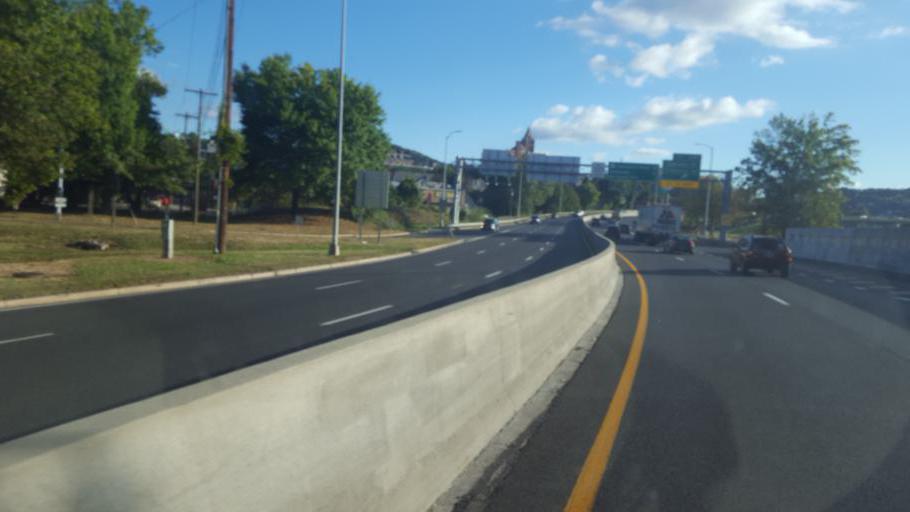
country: US
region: Maryland
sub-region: Allegany County
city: Cumberland
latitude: 39.6475
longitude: -78.7700
